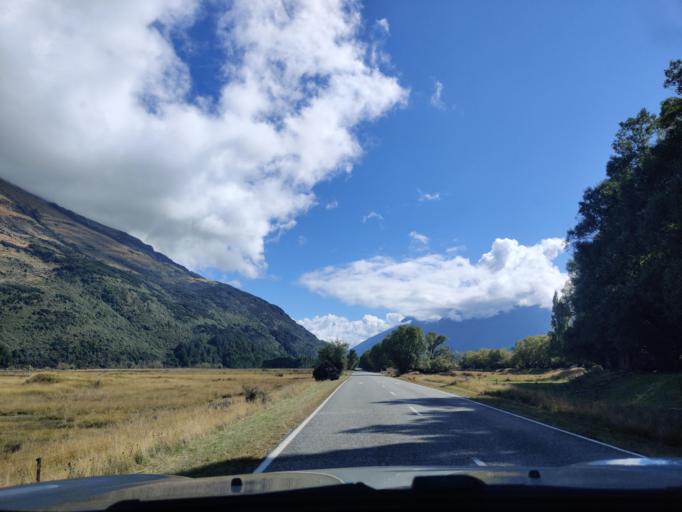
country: NZ
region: Otago
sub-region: Queenstown-Lakes District
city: Queenstown
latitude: -44.7846
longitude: 168.3950
